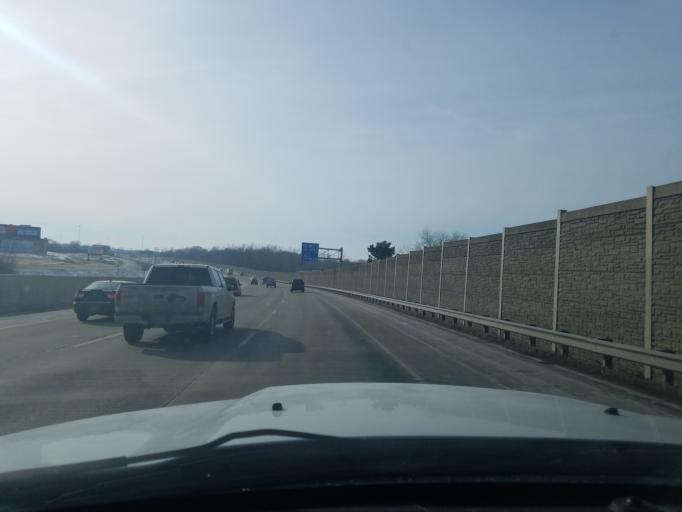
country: US
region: Indiana
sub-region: Allen County
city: Fort Wayne
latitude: 41.1286
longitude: -85.1767
